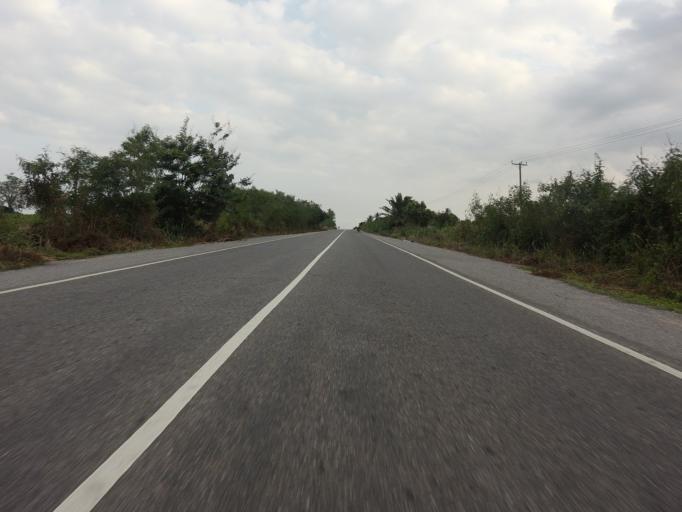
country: GH
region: Volta
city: Ho
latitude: 6.2514
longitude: 0.5507
